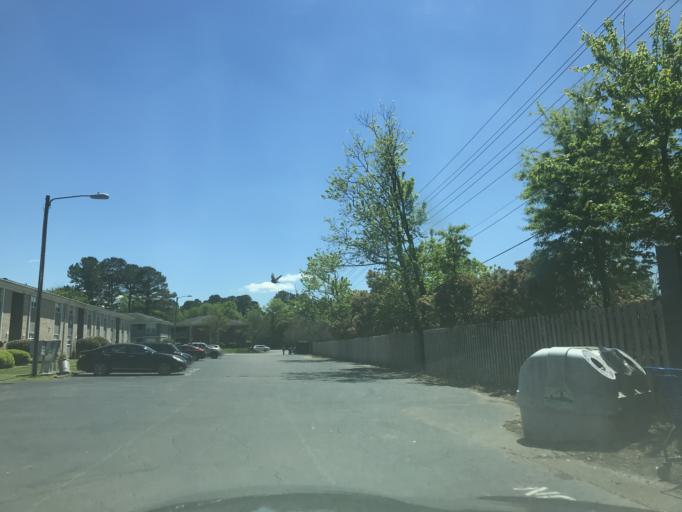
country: US
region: North Carolina
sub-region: Wake County
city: Raleigh
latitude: 35.8465
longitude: -78.5781
